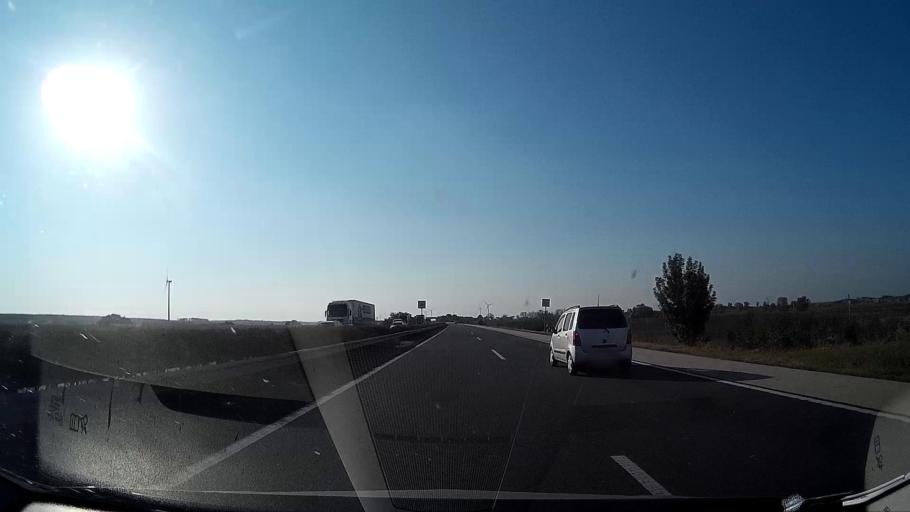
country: HU
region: Komarom-Esztergom
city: Acs
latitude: 47.6827
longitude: 18.0113
